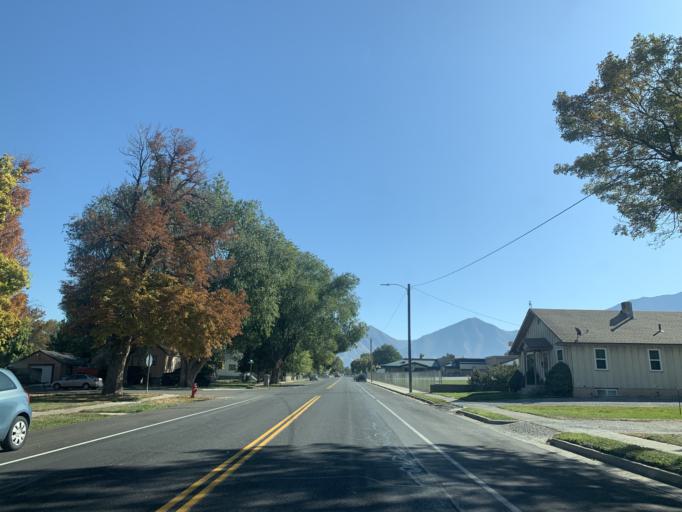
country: US
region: Utah
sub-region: Utah County
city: Payson
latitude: 40.0436
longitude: -111.7432
